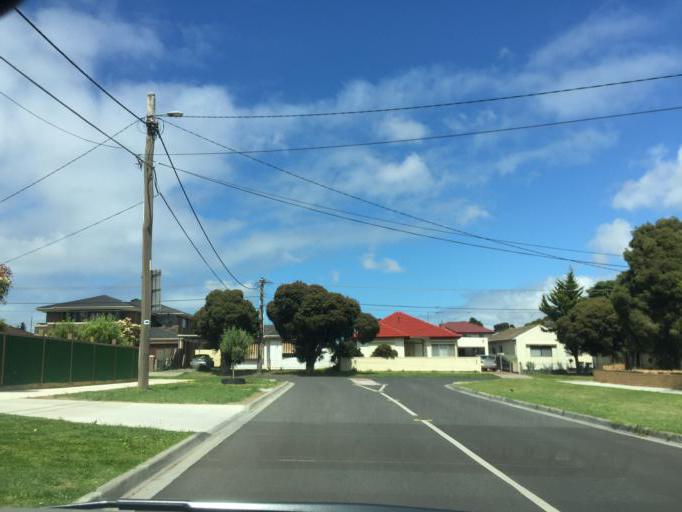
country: AU
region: Victoria
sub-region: Brimbank
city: Albion
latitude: -37.7764
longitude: 144.8431
